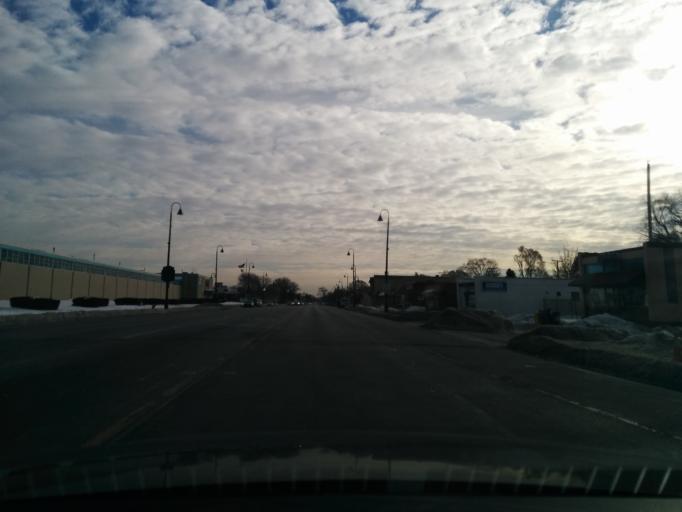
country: US
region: Illinois
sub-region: Cook County
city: Berkeley
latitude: 41.8892
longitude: -87.9031
